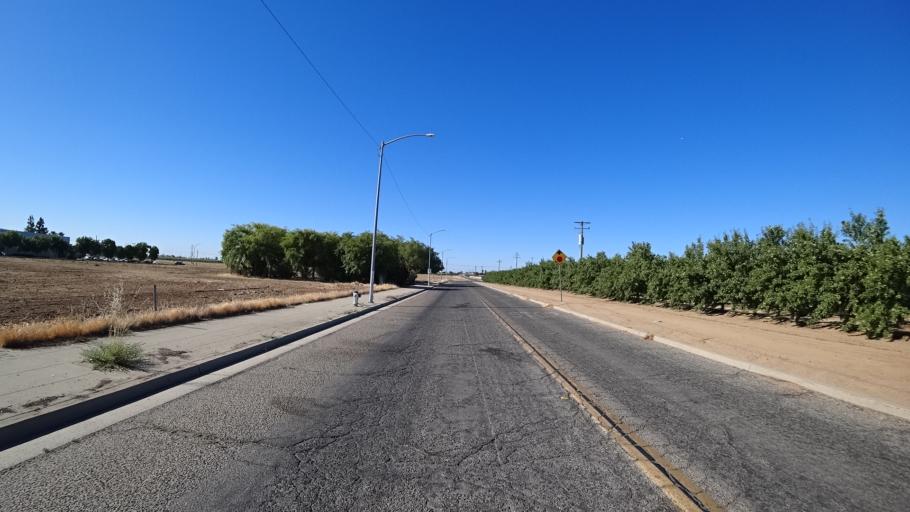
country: US
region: California
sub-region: Fresno County
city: West Park
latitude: 36.7154
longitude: -119.8267
